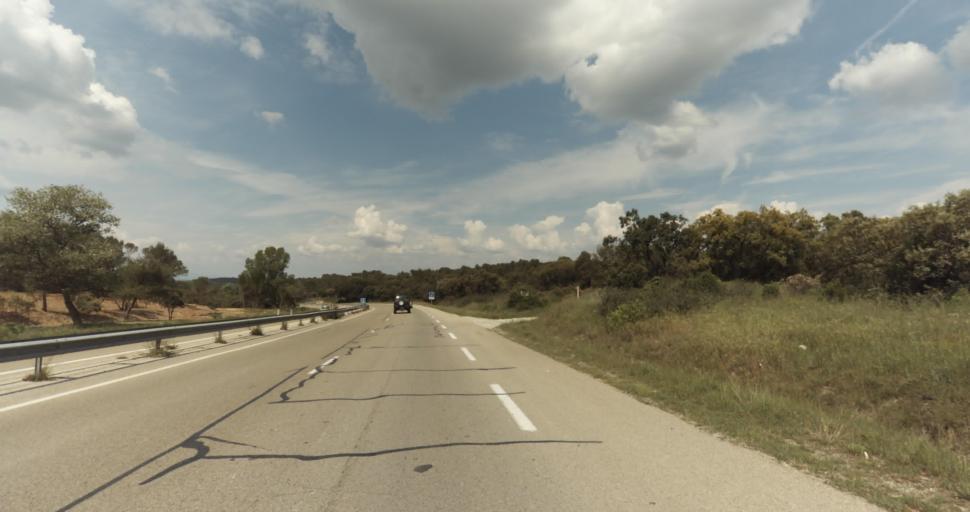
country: FR
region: Languedoc-Roussillon
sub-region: Departement du Gard
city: La Calmette
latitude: 43.8822
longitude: 4.3084
